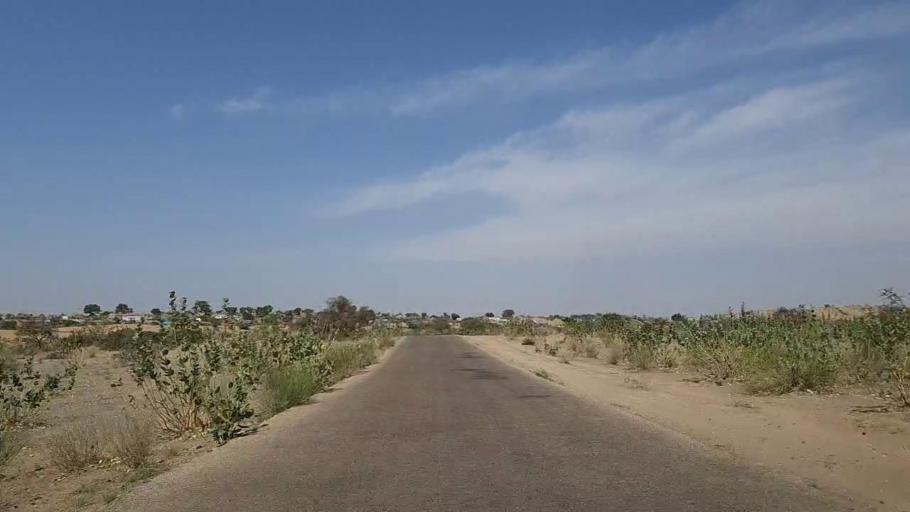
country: PK
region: Sindh
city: Umarkot
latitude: 25.1478
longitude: 70.0133
